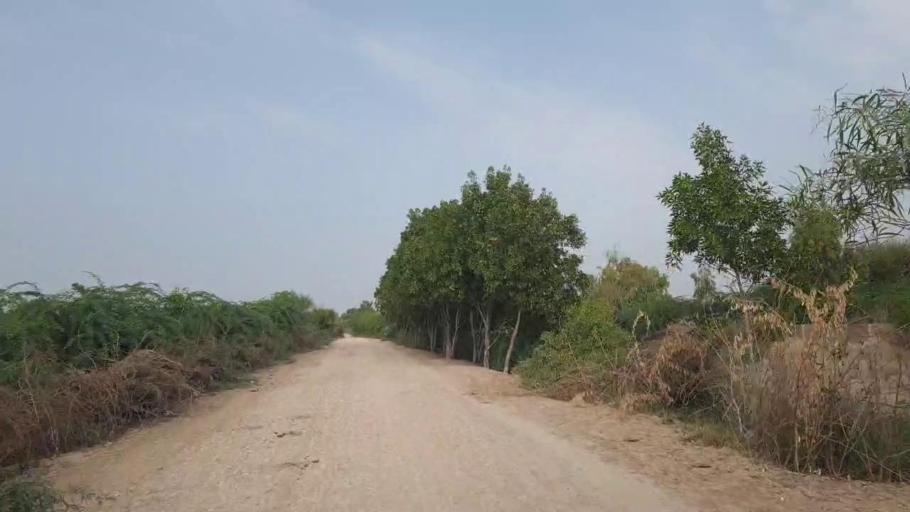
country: PK
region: Sindh
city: Badin
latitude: 24.5932
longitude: 68.7413
